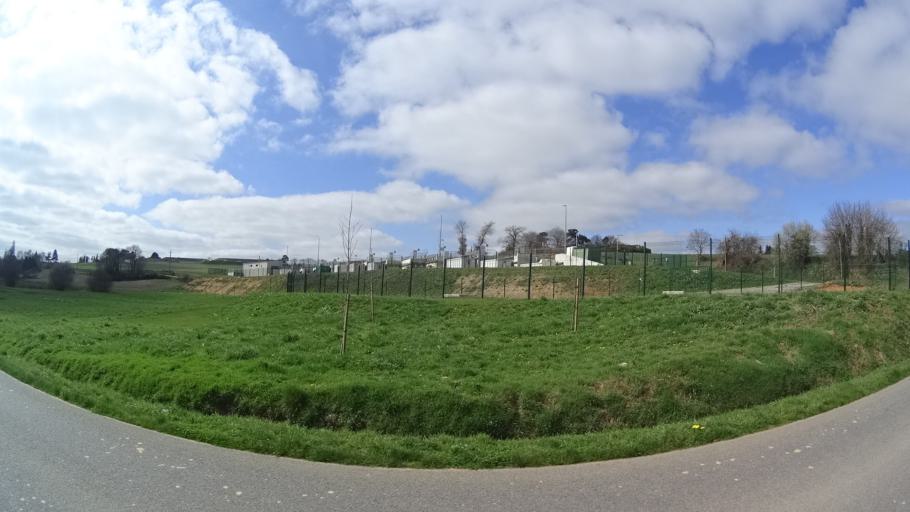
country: FR
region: Brittany
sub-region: Departement du Morbihan
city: Caro
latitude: 47.8331
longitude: -2.3112
